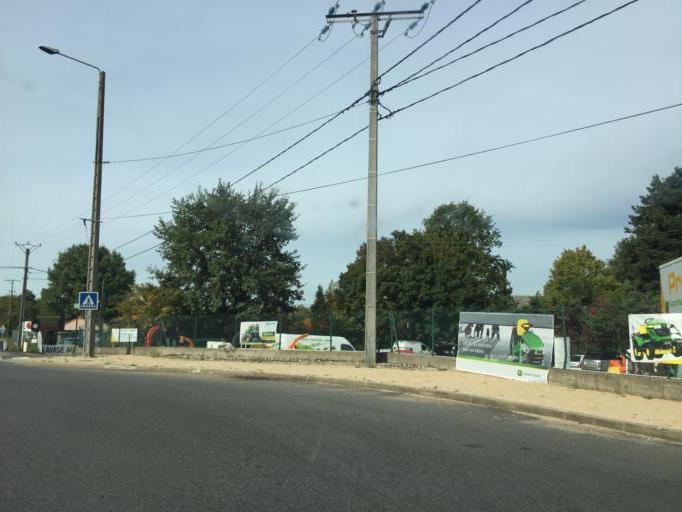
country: FR
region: Rhone-Alpes
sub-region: Departement du Rhone
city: Lissieu
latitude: 45.8711
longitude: 4.7452
